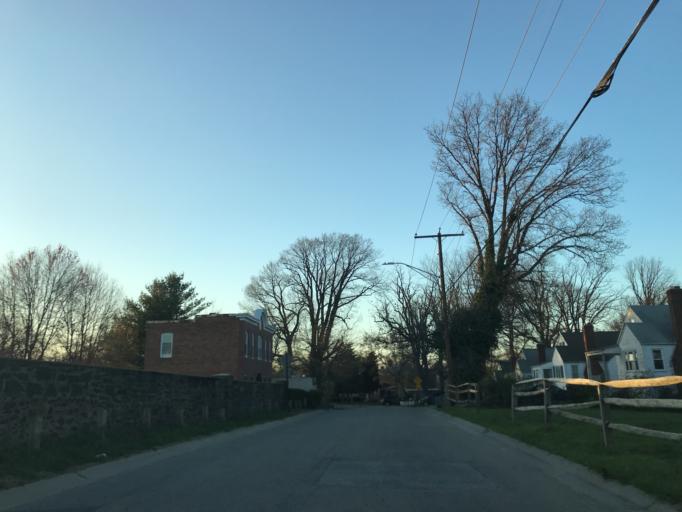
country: US
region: Maryland
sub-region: Baltimore County
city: Parkville
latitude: 39.3393
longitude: -76.5607
